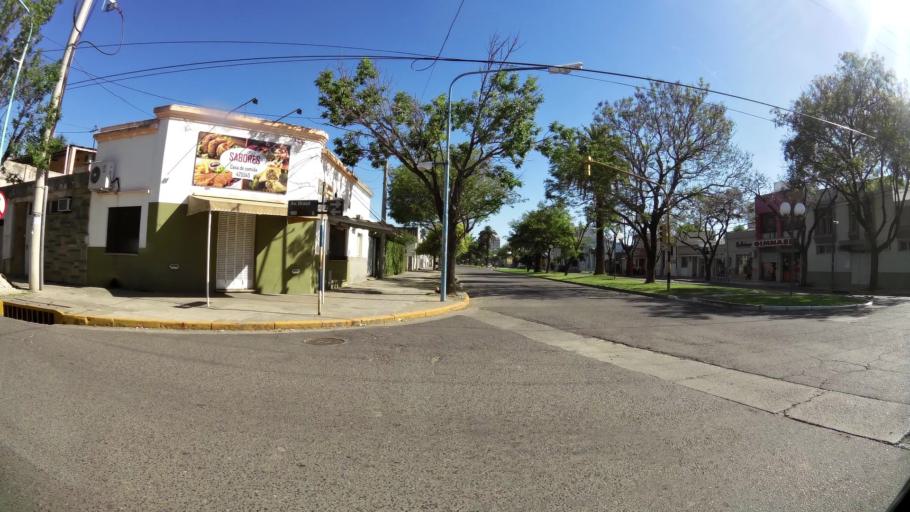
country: AR
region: Santa Fe
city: Rafaela
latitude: -31.2434
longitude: -61.4894
